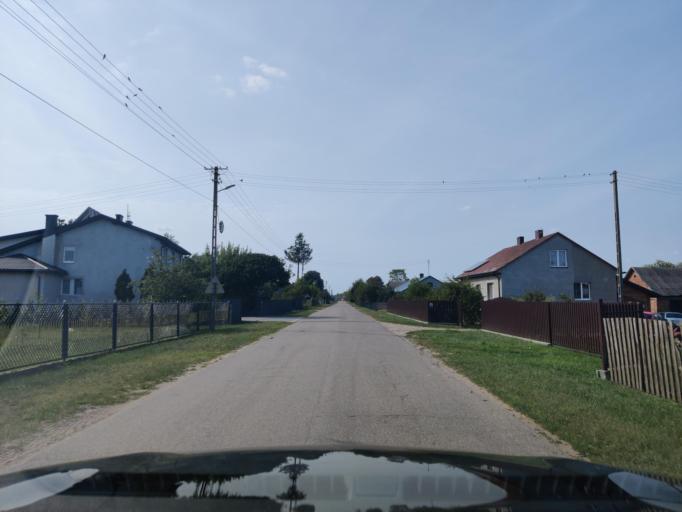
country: PL
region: Masovian Voivodeship
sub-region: Powiat pultuski
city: Obryte
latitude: 52.7601
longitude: 21.3035
